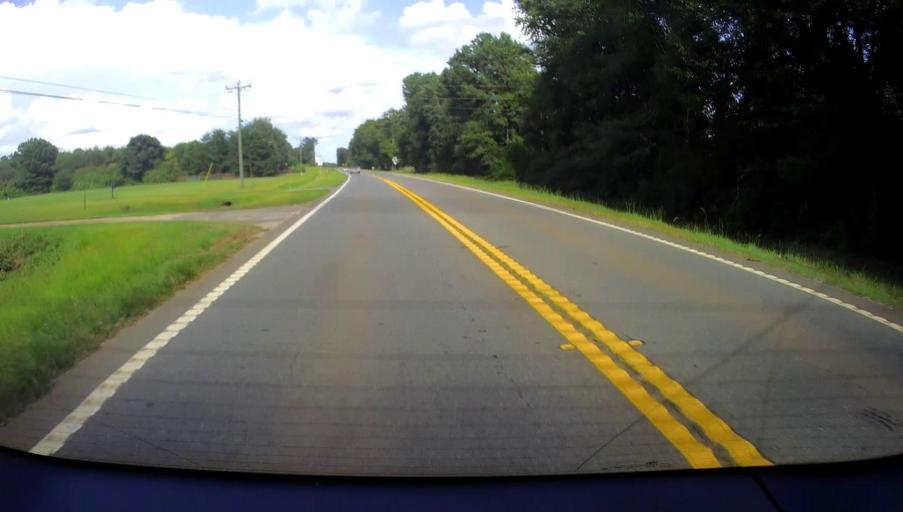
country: US
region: Georgia
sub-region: Meriwether County
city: Manchester
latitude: 32.9904
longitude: -84.5249
